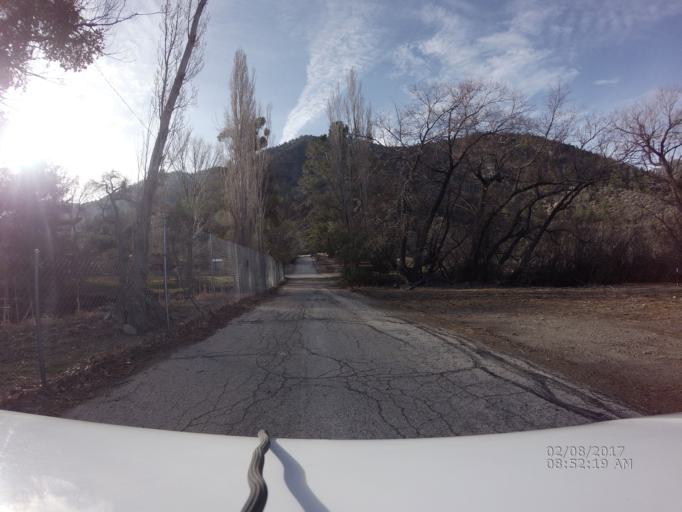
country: US
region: California
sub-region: San Bernardino County
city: Pinon Hills
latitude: 34.3962
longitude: -117.8085
